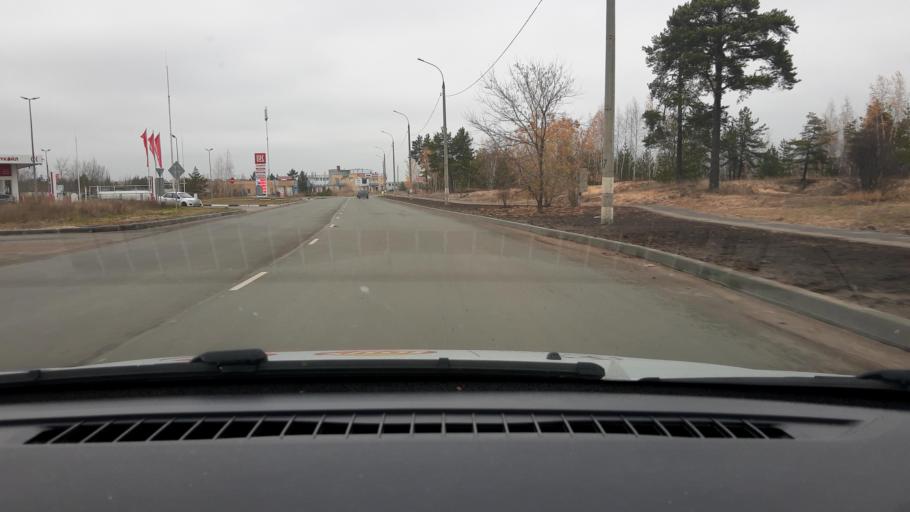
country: RU
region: Nizjnij Novgorod
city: Dzerzhinsk
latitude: 56.2364
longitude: 43.4080
